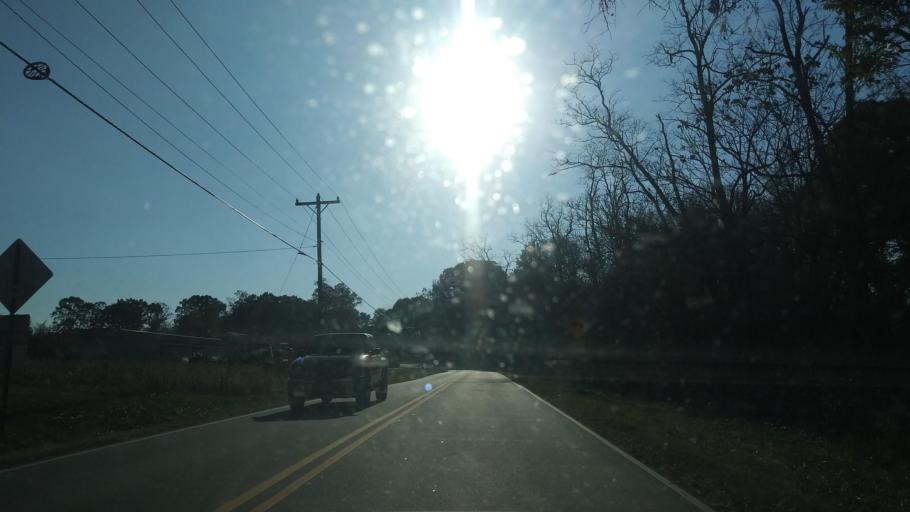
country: US
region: North Carolina
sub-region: Guilford County
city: McLeansville
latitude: 36.2119
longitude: -79.7142
